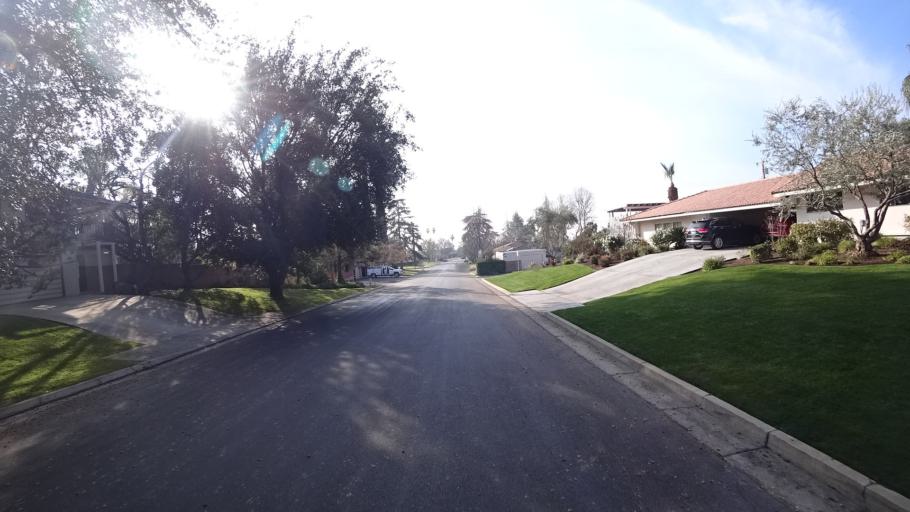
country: US
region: California
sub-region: Kern County
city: Oildale
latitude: 35.4095
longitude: -118.9795
